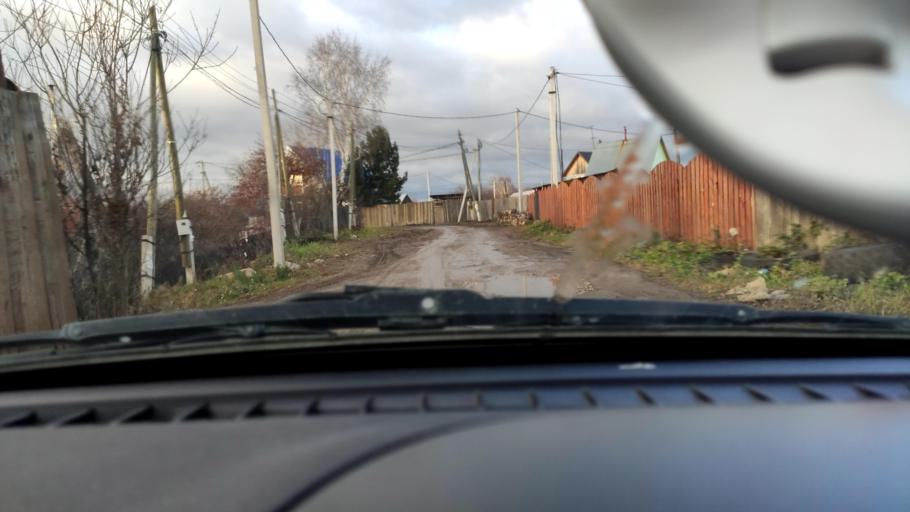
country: RU
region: Perm
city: Kondratovo
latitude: 57.9565
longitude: 56.1459
